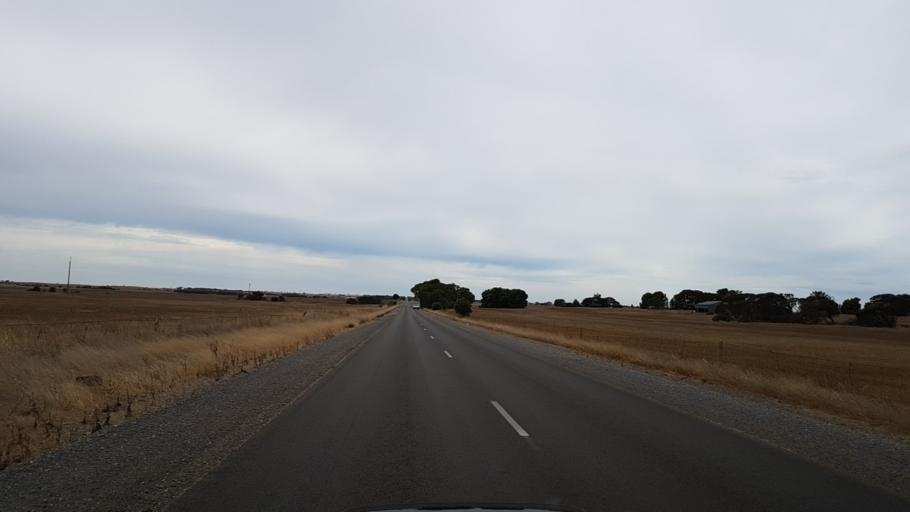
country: AU
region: South Australia
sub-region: Yorke Peninsula
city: Honiton
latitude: -34.9849
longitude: 137.3205
